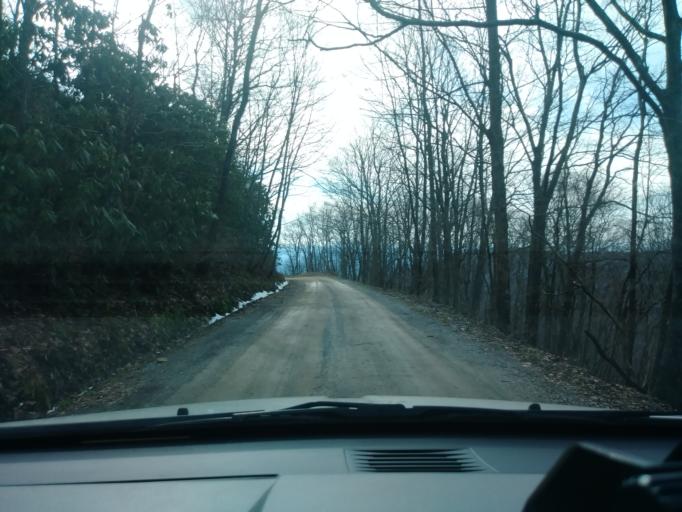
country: US
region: Tennessee
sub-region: Greene County
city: Tusculum
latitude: 36.0269
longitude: -82.7197
